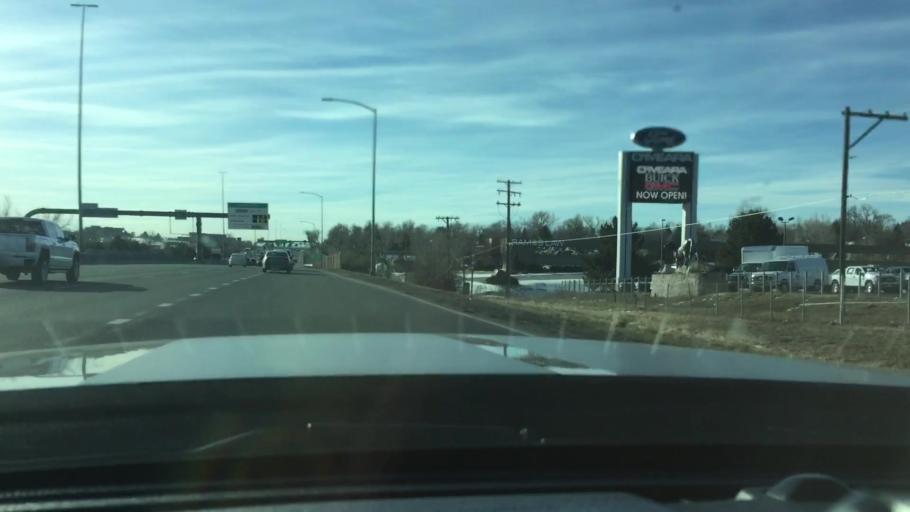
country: US
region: Colorado
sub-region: Adams County
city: Northglenn
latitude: 39.8825
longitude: -104.9880
